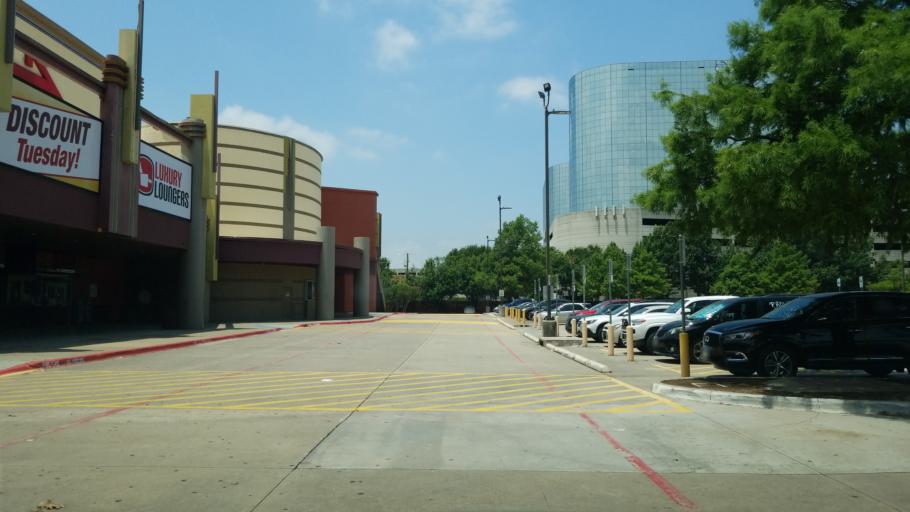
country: US
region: Texas
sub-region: Dallas County
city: Farmers Branch
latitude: 32.9107
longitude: -96.8742
